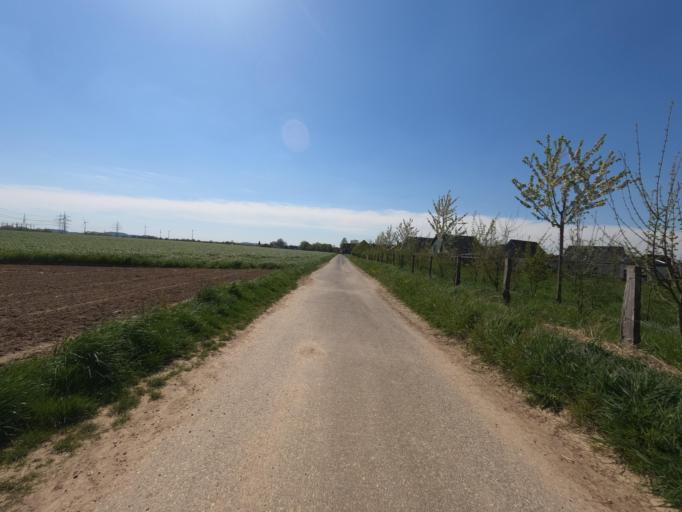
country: DE
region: North Rhine-Westphalia
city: Siersdorf
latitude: 50.9239
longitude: 6.2176
